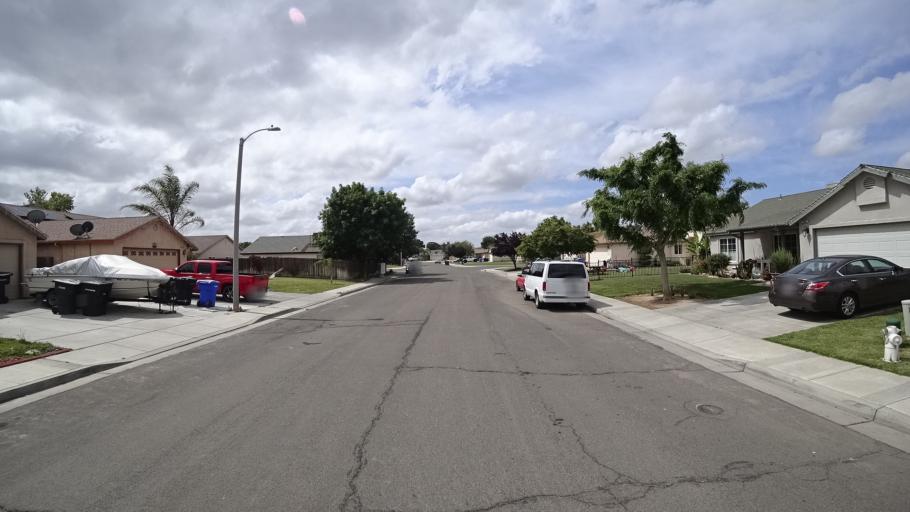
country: US
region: California
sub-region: Kings County
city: Hanford
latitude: 36.3082
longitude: -119.6635
